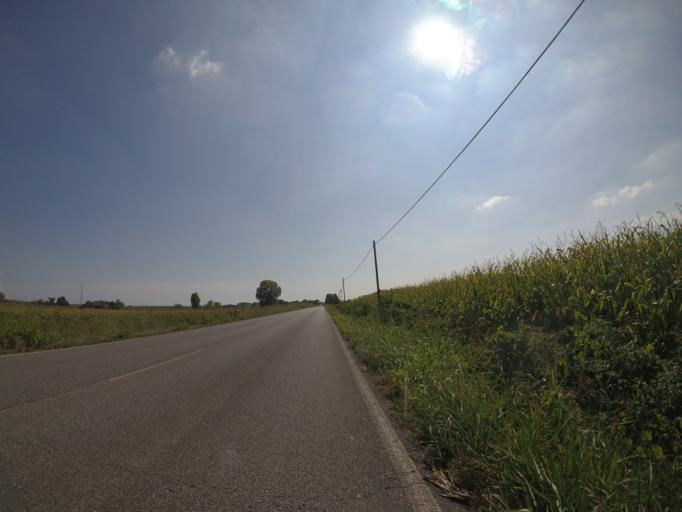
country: IT
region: Friuli Venezia Giulia
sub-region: Provincia di Udine
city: Pocenia
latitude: 45.8164
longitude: 13.1016
